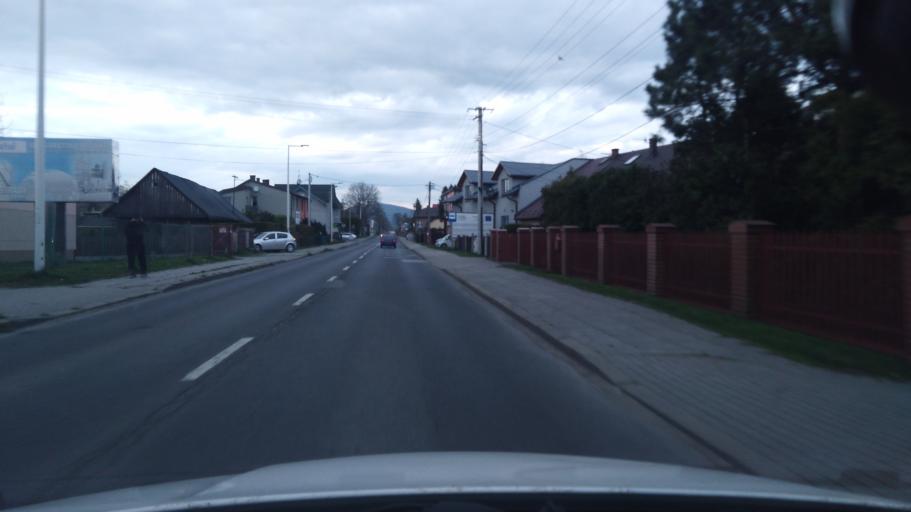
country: PL
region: Silesian Voivodeship
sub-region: Powiat zywiecki
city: Wieprz
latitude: 49.6678
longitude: 19.1786
